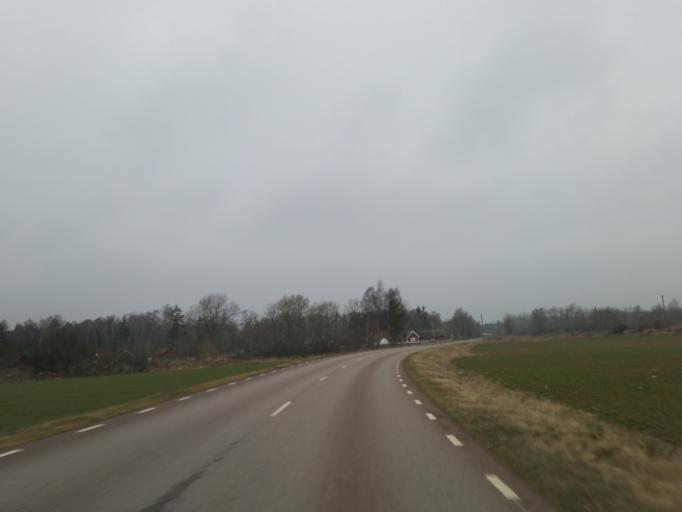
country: SE
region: Kalmar
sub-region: Morbylanga Kommun
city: Sodra Sandby
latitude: 56.6152
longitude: 16.6104
